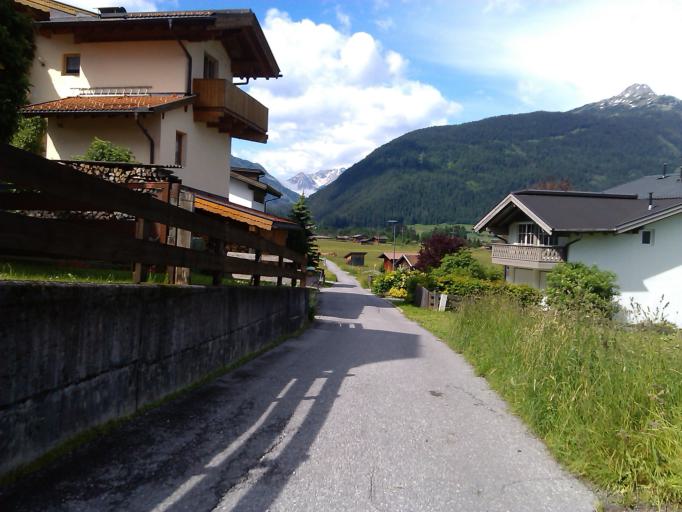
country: AT
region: Tyrol
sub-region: Politischer Bezirk Reutte
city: Ehrwald
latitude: 47.3994
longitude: 10.9171
